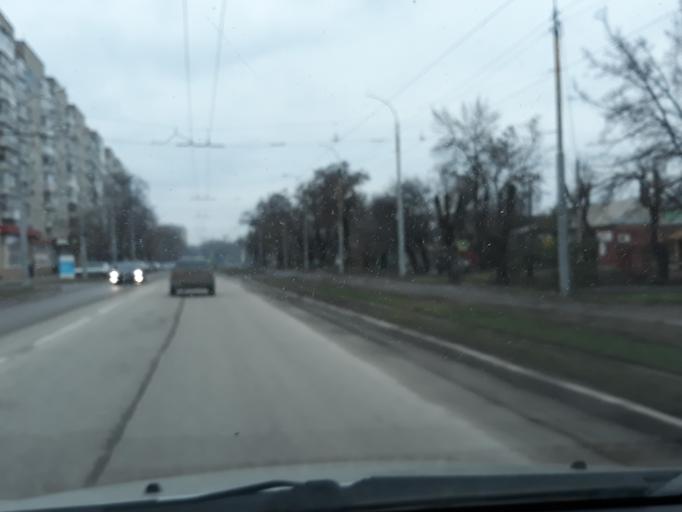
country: RU
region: Rostov
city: Taganrog
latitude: 47.2271
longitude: 38.9109
